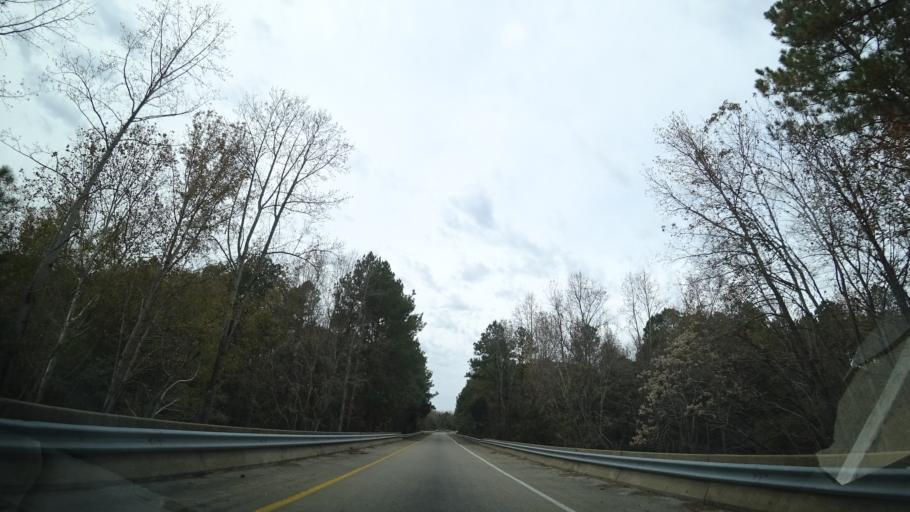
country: US
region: Virginia
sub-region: Hanover County
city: Mechanicsville
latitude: 37.6102
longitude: -77.3600
